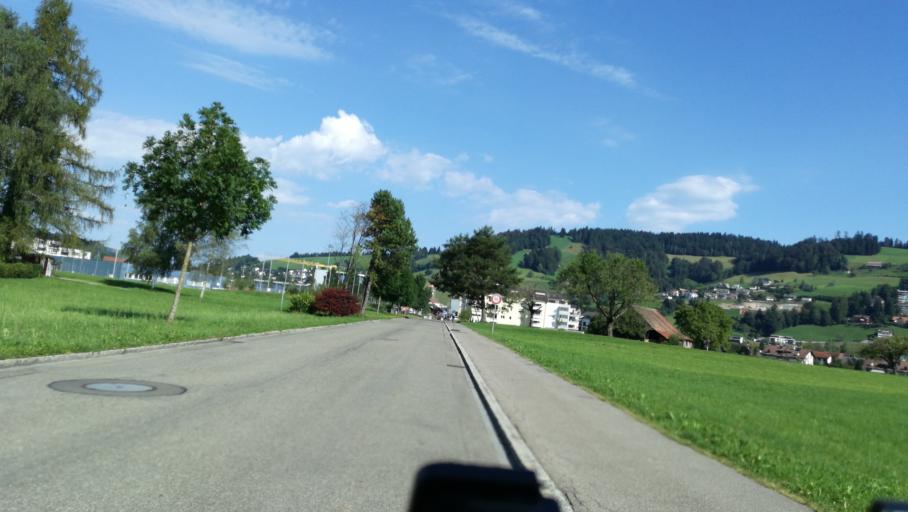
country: CH
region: Zug
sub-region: Zug
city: Unterageri
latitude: 47.1299
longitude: 8.5886
